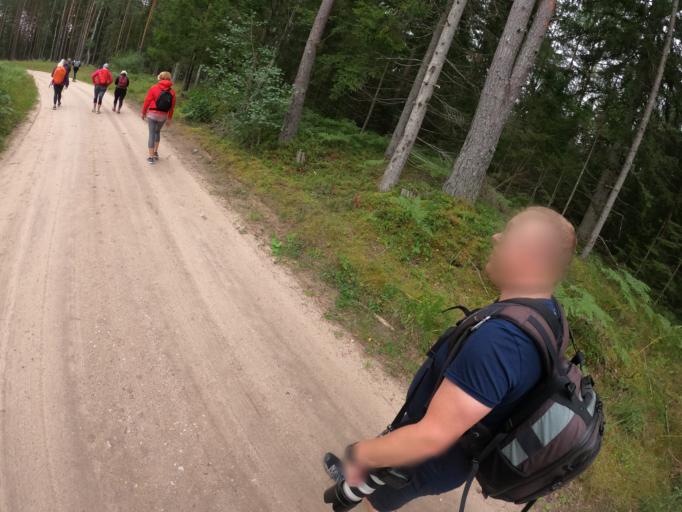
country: LV
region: Kuldigas Rajons
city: Kuldiga
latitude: 57.0185
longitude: 22.0019
